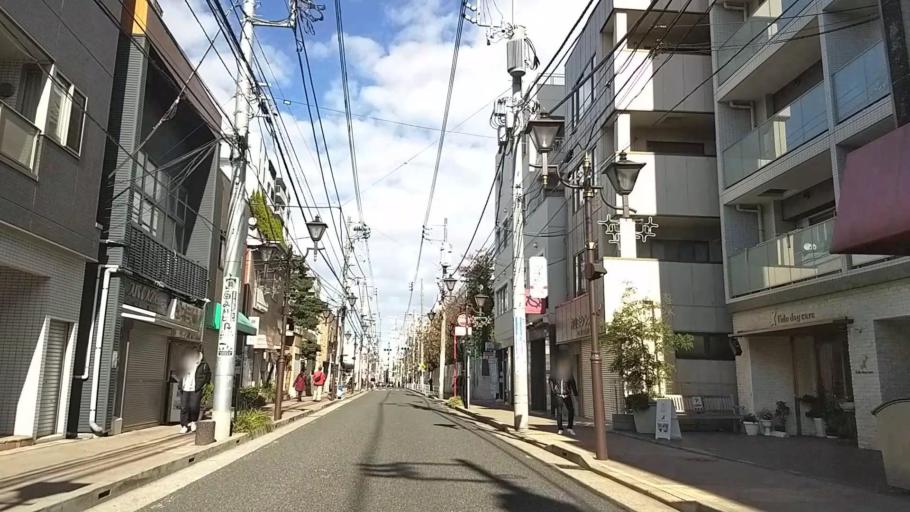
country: JP
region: Kanagawa
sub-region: Kawasaki-shi
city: Kawasaki
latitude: 35.5114
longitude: 139.6746
